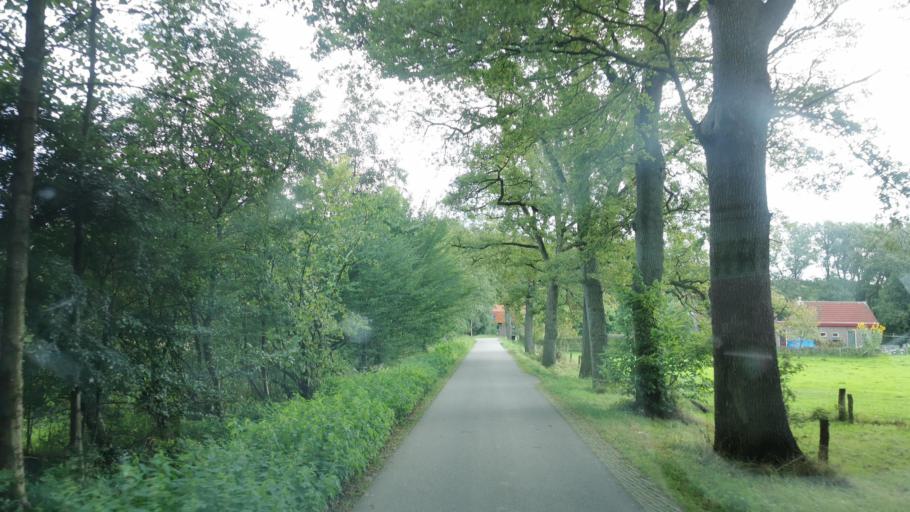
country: NL
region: Overijssel
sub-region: Gemeente Oldenzaal
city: Oldenzaal
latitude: 52.3095
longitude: 6.9484
